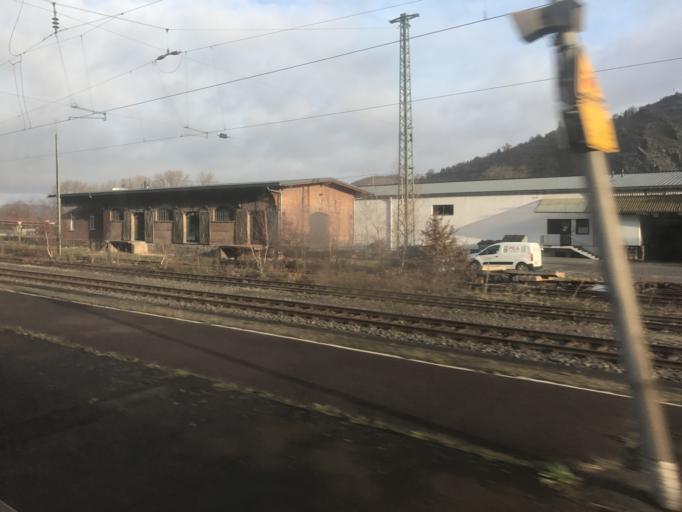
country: DE
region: Rheinland-Pfalz
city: Brohl-Lutzing
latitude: 50.4809
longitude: 7.3335
